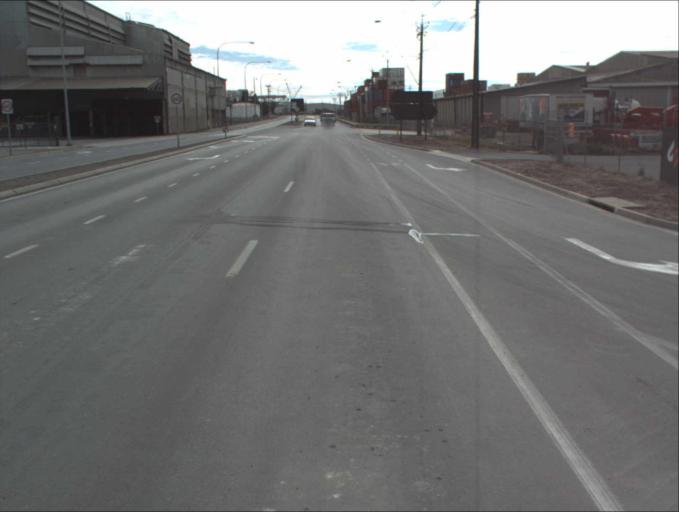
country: AU
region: South Australia
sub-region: Port Adelaide Enfield
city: Birkenhead
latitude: -34.8408
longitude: 138.5149
